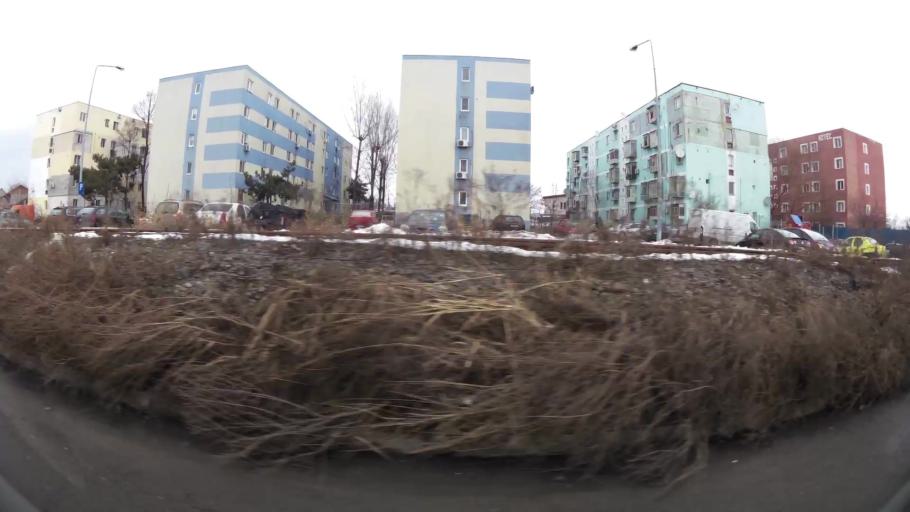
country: RO
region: Ilfov
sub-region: Comuna Glina
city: Catelu
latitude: 44.4266
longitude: 26.2175
